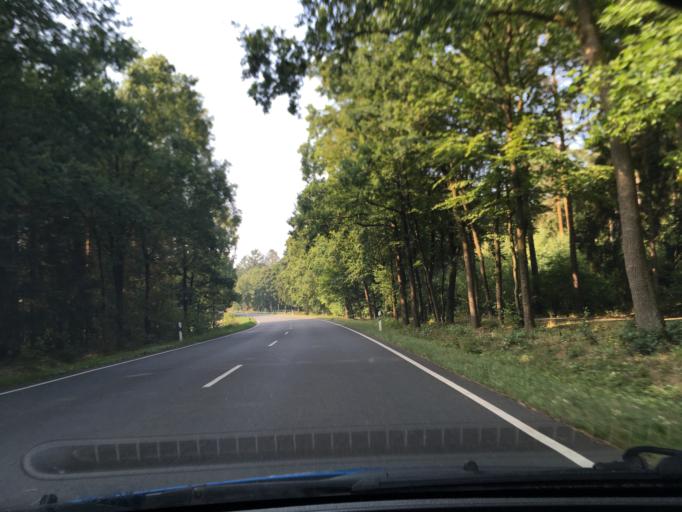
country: DE
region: Lower Saxony
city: Bispingen
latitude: 53.0329
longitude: 9.9787
